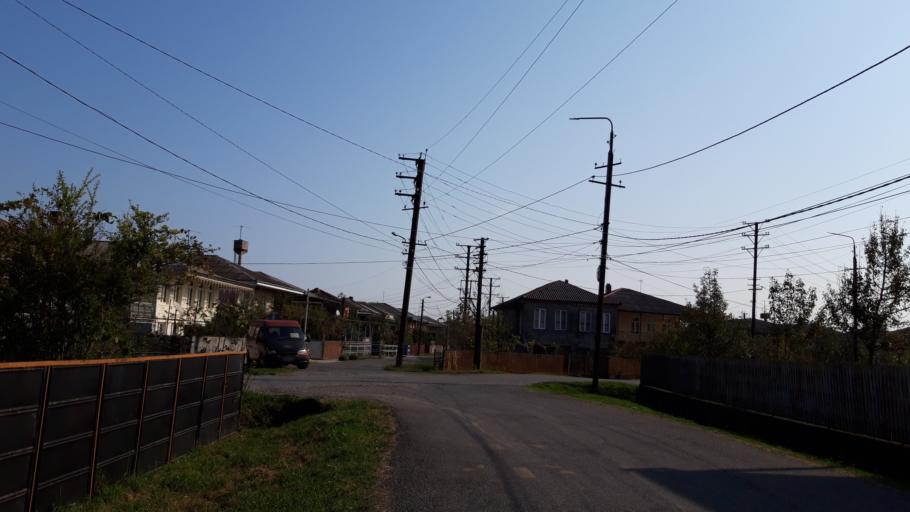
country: GE
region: Imereti
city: Samtredia
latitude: 42.1631
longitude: 42.3328
